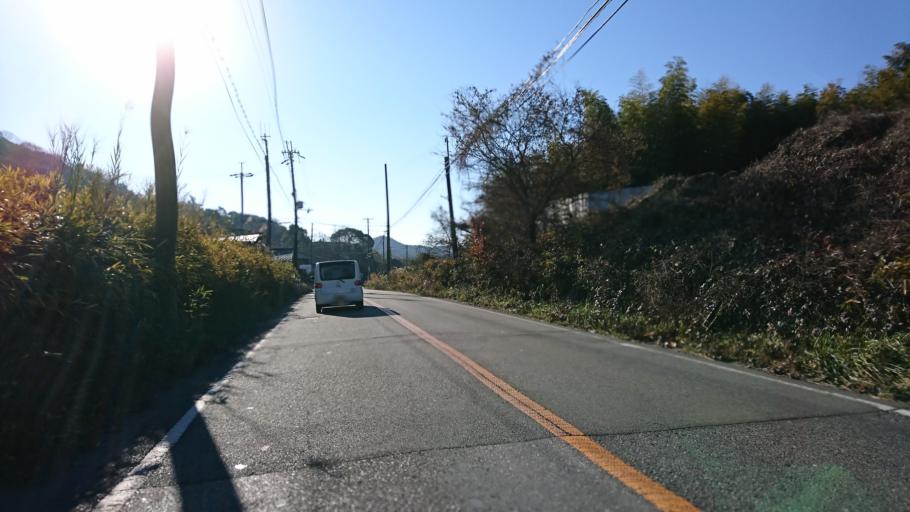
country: JP
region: Hyogo
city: Kakogawacho-honmachi
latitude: 34.8211
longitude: 134.8352
